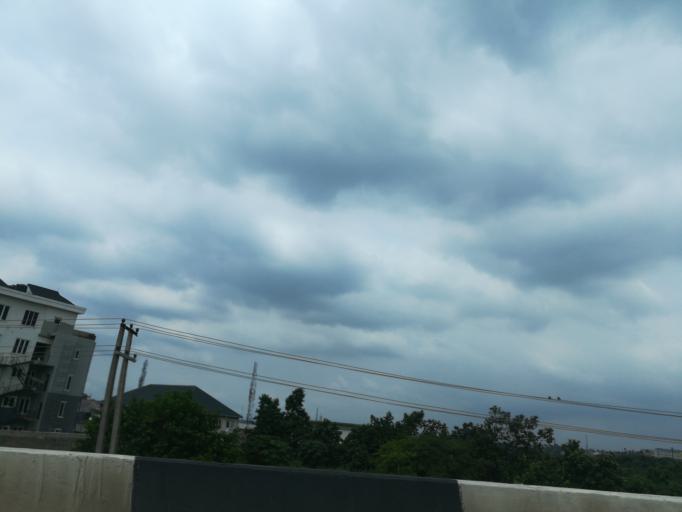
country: NG
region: Lagos
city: Ojota
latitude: 6.5651
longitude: 3.3958
